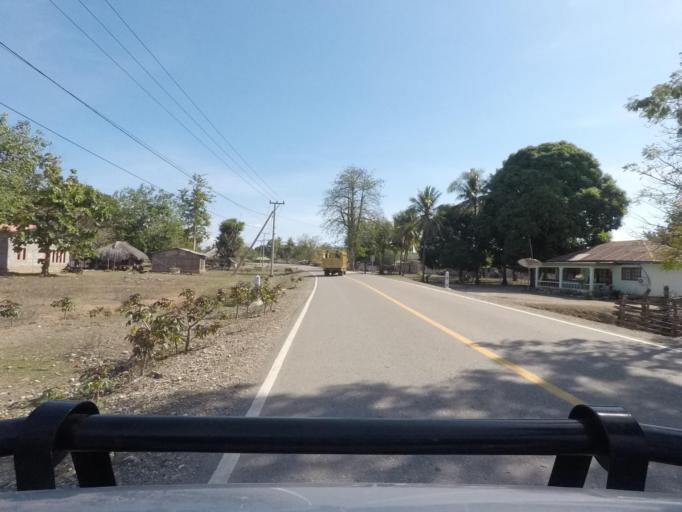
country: TL
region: Bobonaro
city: Maliana
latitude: -8.8951
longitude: 125.0041
